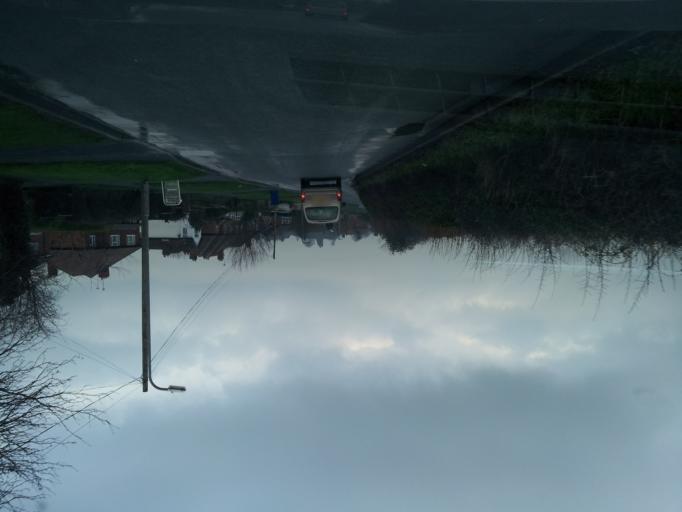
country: GB
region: England
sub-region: Staffordshire
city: Burton upon Trent
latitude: 52.8519
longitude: -1.6942
